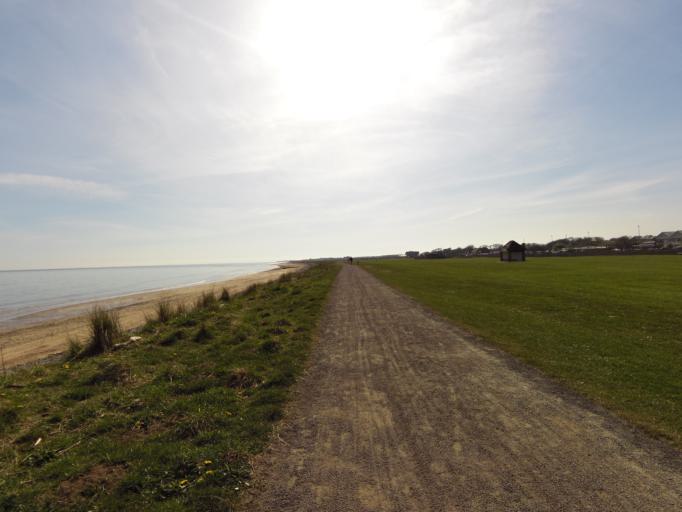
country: GB
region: Scotland
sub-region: Angus
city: Arbroath
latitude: 56.5484
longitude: -2.6112
